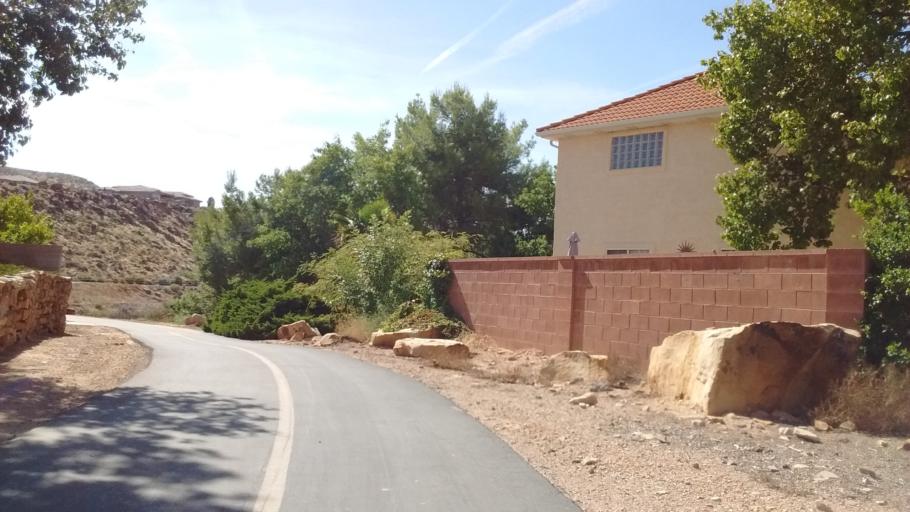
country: US
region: Utah
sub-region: Washington County
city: Saint George
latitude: 37.0729
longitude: -113.5775
